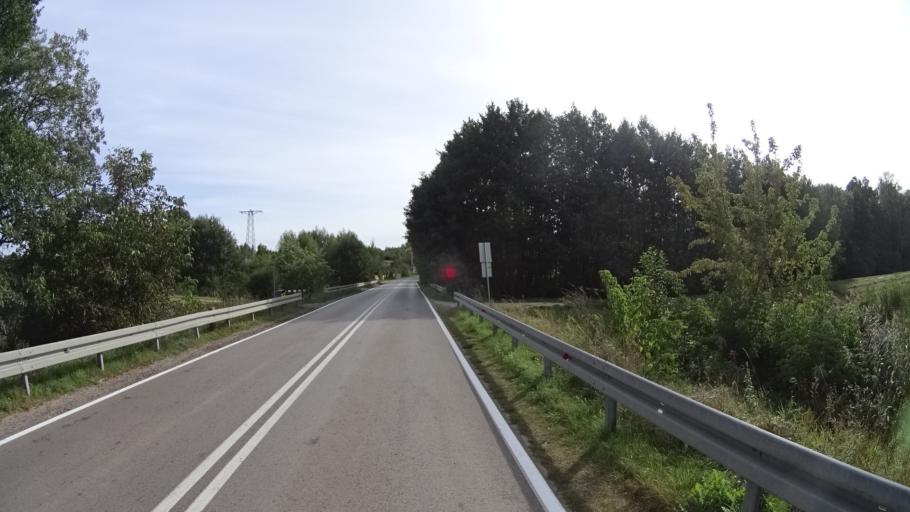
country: PL
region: Masovian Voivodeship
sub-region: Powiat legionowski
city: Serock
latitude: 52.4769
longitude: 21.0926
